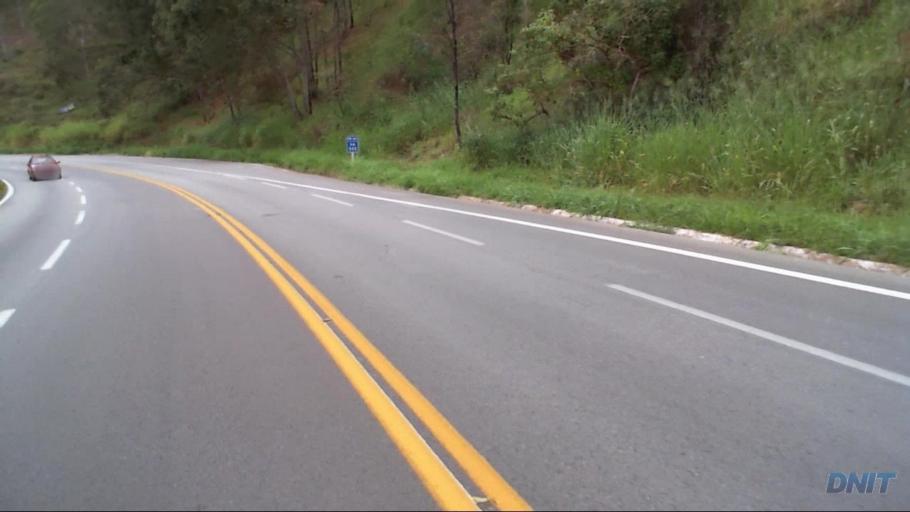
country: BR
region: Minas Gerais
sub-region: Joao Monlevade
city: Joao Monlevade
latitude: -19.8441
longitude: -43.1026
